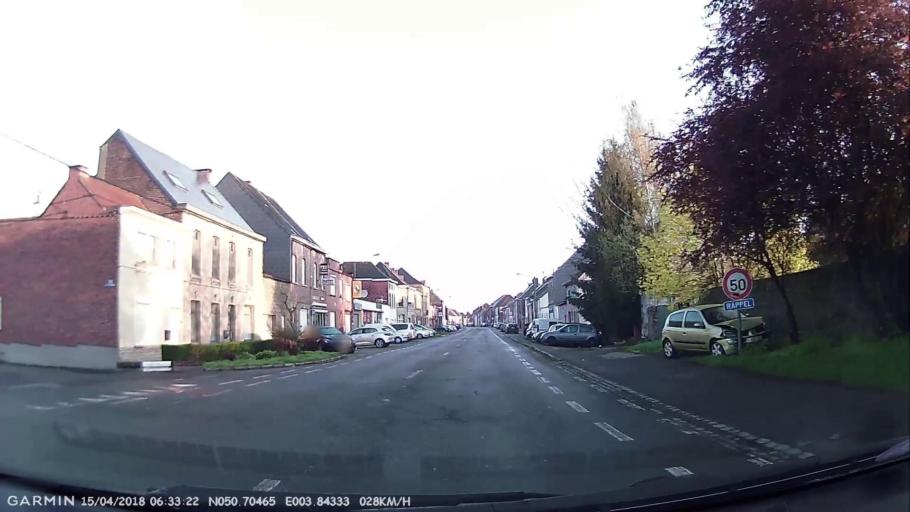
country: BE
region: Wallonia
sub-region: Province du Hainaut
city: Lessines
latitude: 50.7047
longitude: 3.8432
